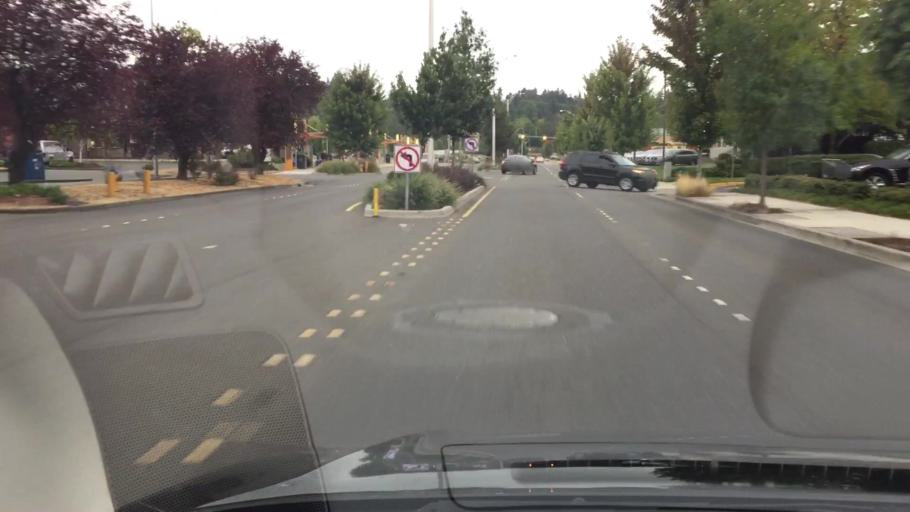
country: US
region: Washington
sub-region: King County
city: Tukwila
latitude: 47.4564
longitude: -122.2544
